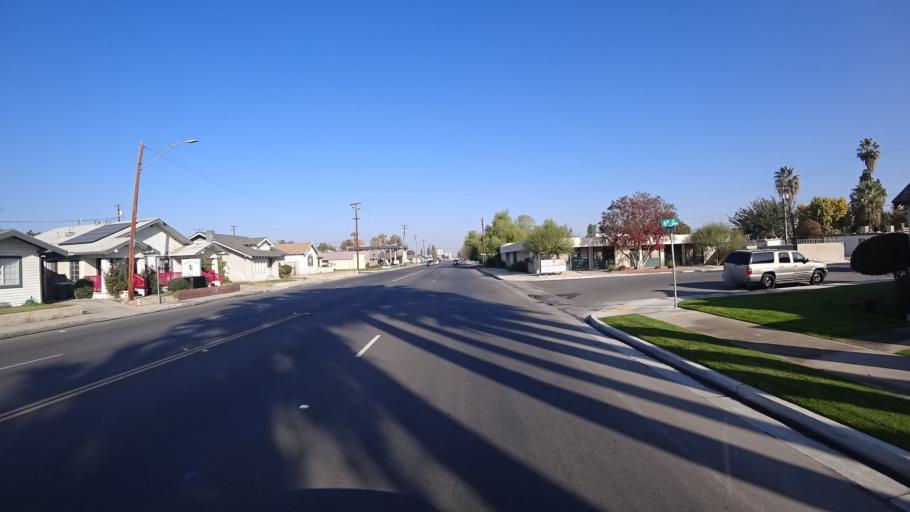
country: US
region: California
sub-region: Kern County
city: Bakersfield
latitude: 35.3625
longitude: -119.0212
